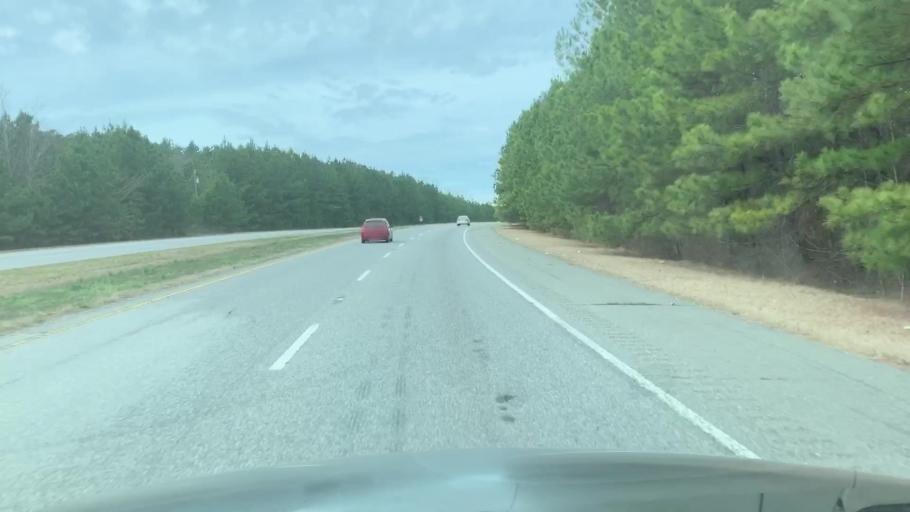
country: US
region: South Carolina
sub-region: Greenville County
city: Golden Grove
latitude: 34.7326
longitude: -82.4249
